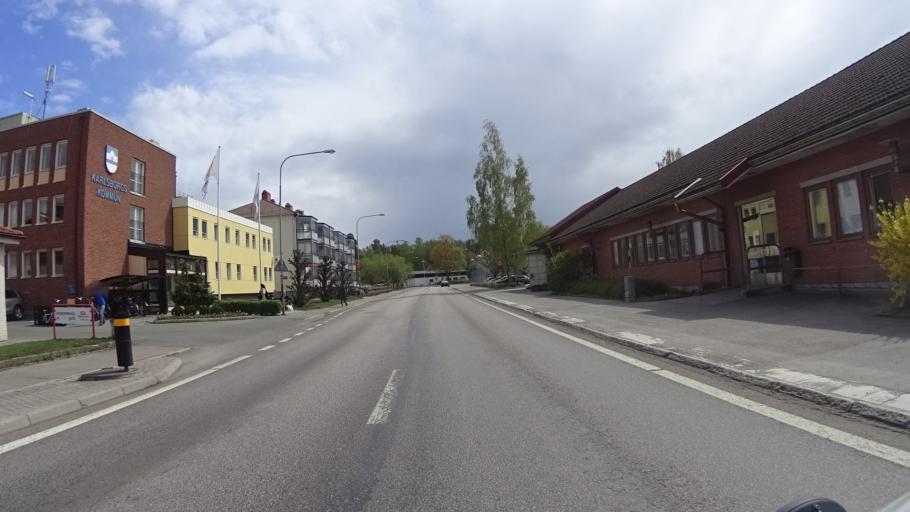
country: SE
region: Vaestra Goetaland
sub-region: Karlsborgs Kommun
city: Karlsborg
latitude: 58.5297
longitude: 14.5110
